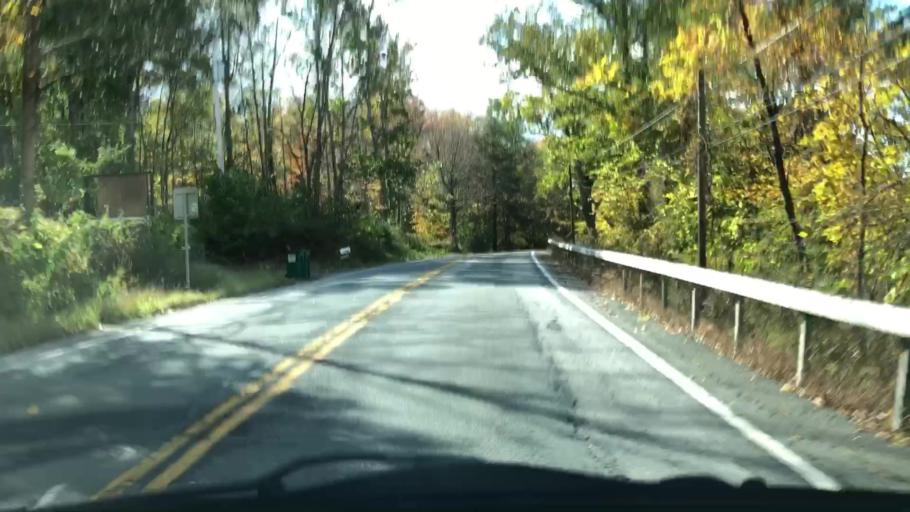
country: US
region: New York
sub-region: Orange County
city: Walden
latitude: 41.5826
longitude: -74.1865
